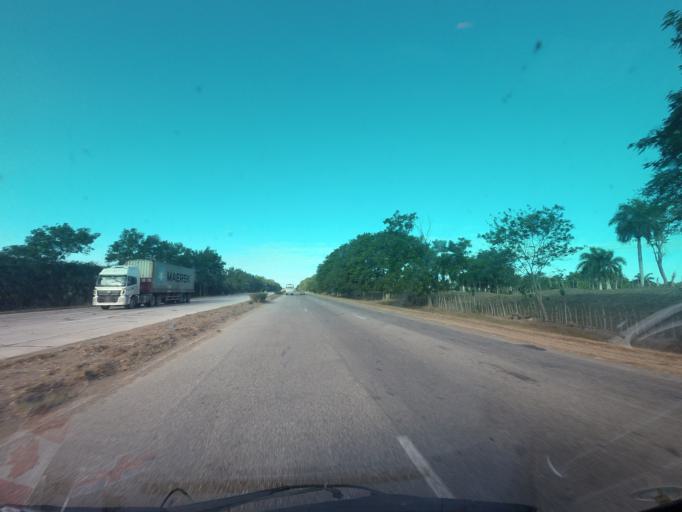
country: CU
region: Cienfuegos
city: Rodas
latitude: 22.4429
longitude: -80.5364
